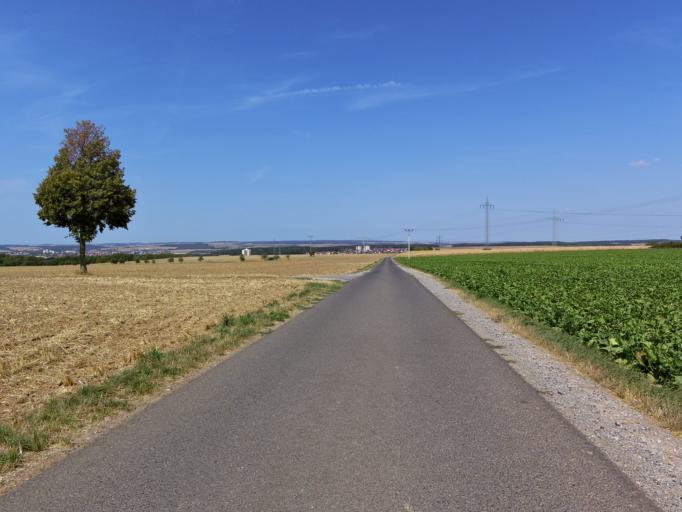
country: DE
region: Bavaria
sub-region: Regierungsbezirk Unterfranken
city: Rottendorf
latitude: 49.7764
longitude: 10.0292
